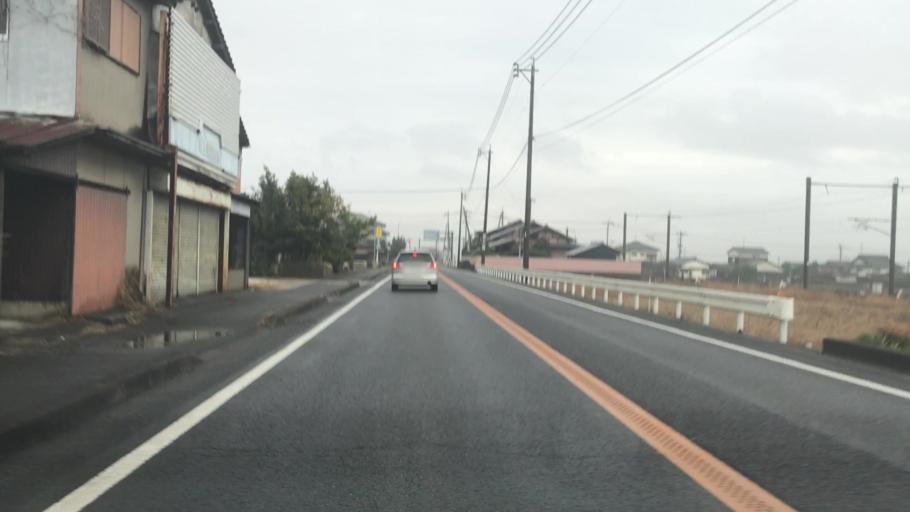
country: JP
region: Saga Prefecture
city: Takeocho-takeo
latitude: 33.2127
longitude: 130.1185
